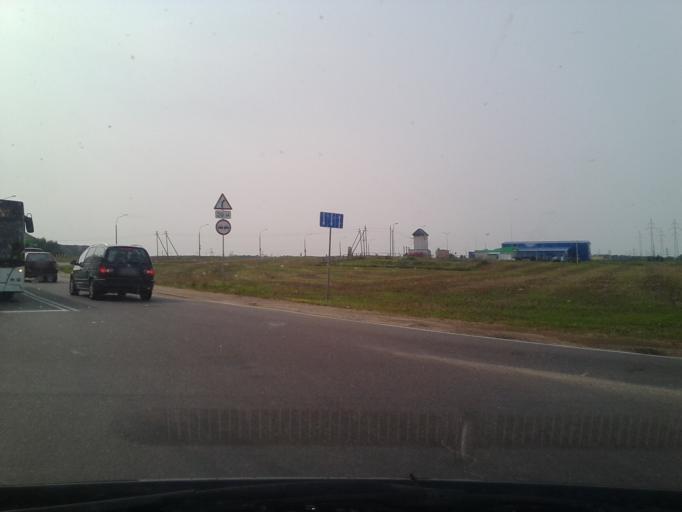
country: BY
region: Minsk
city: Machulishchy
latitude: 53.8314
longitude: 27.6113
